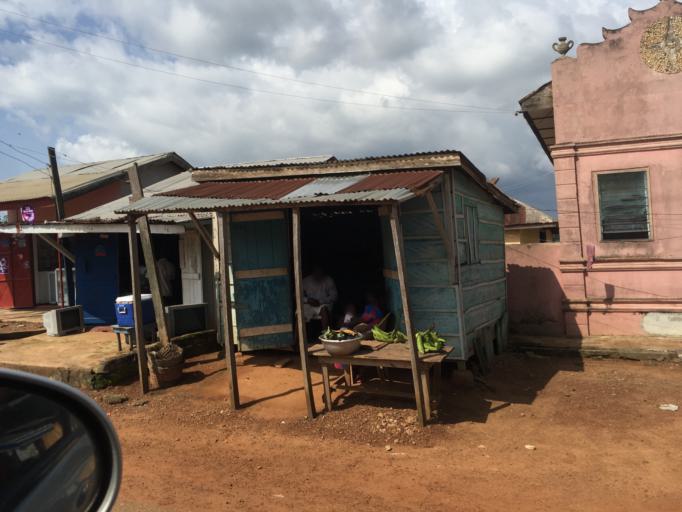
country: GH
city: Mpraeso
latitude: 6.5948
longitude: -0.7367
